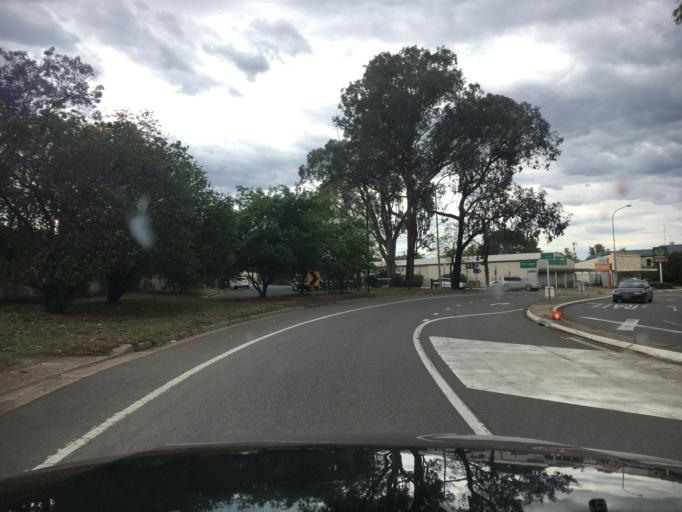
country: AU
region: New South Wales
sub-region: Muswellbrook
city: Muswellbrook
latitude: -32.0459
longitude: 150.8682
